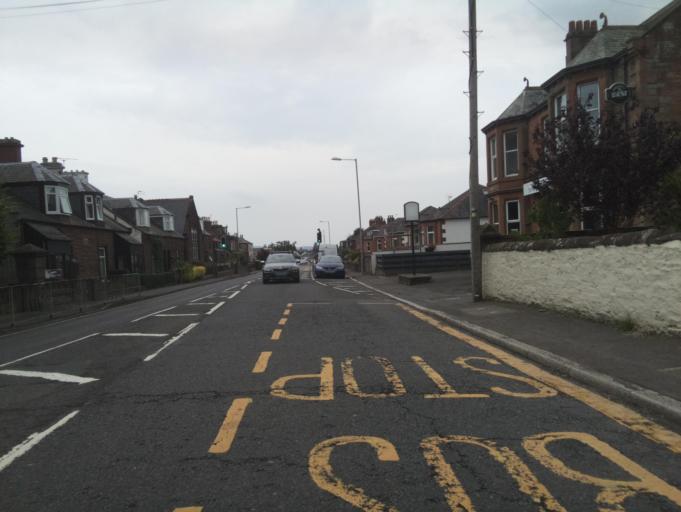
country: GB
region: Scotland
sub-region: Dumfries and Galloway
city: Dumfries
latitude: 55.0693
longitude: -3.5846
